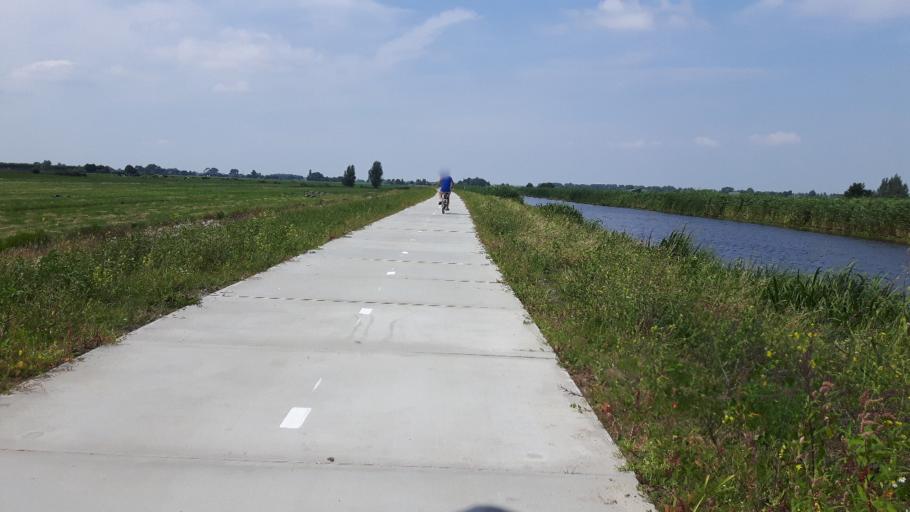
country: NL
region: South Holland
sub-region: Molenwaard
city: Liesveld
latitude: 51.8920
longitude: 4.8575
